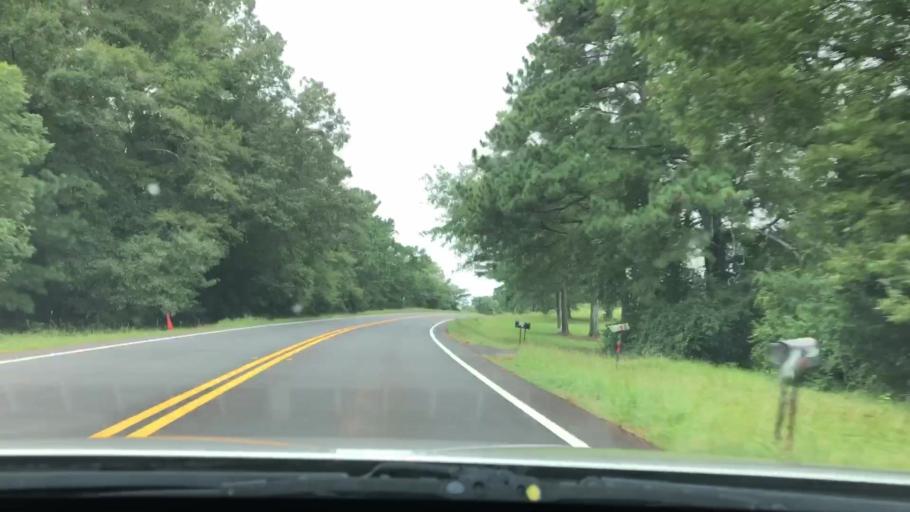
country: US
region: Georgia
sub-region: Upson County
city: Hannahs Mill
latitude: 33.0115
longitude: -84.4591
